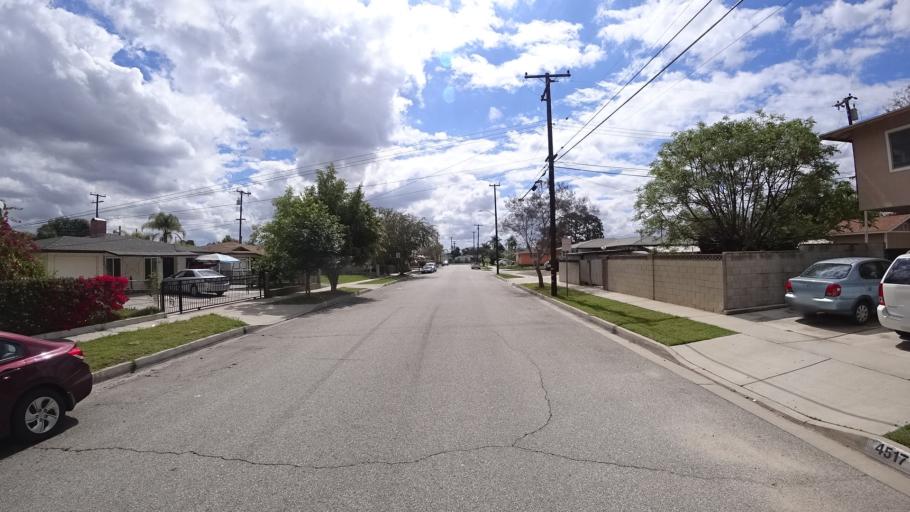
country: US
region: California
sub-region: Los Angeles County
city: Baldwin Park
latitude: 34.0942
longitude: -117.9803
